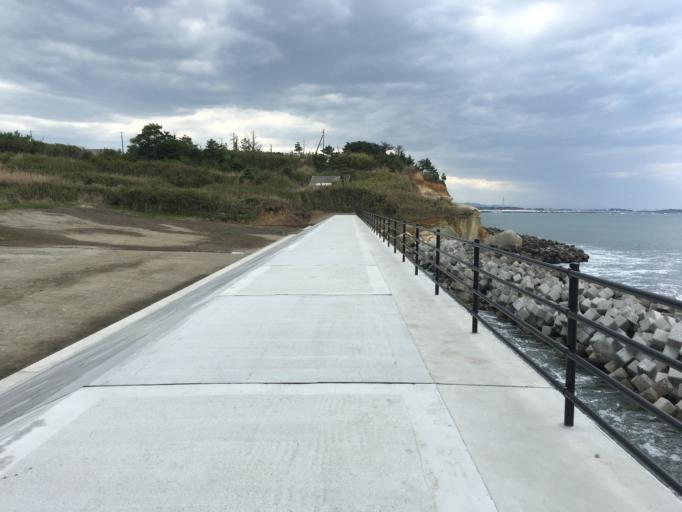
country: JP
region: Miyagi
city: Marumori
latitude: 37.7632
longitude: 140.9969
